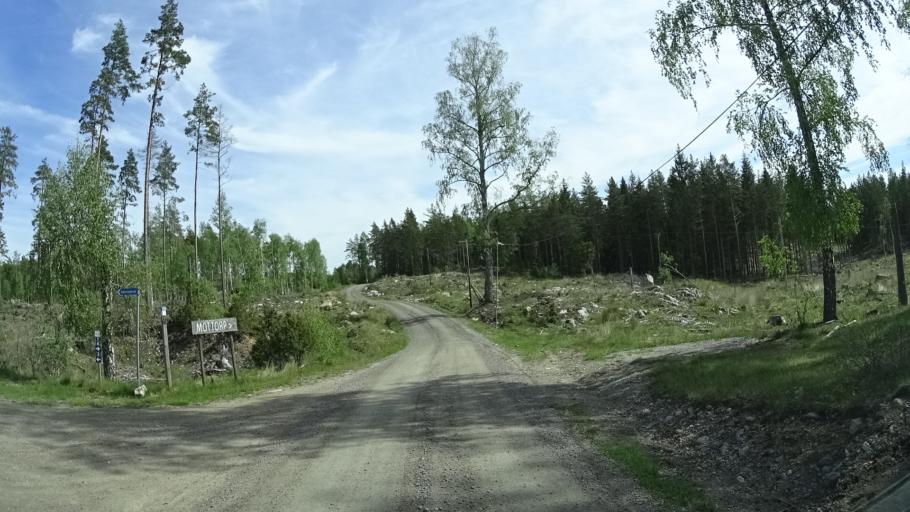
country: SE
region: OEstergoetland
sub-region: Finspangs Kommun
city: Finspang
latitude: 58.7709
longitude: 15.8492
